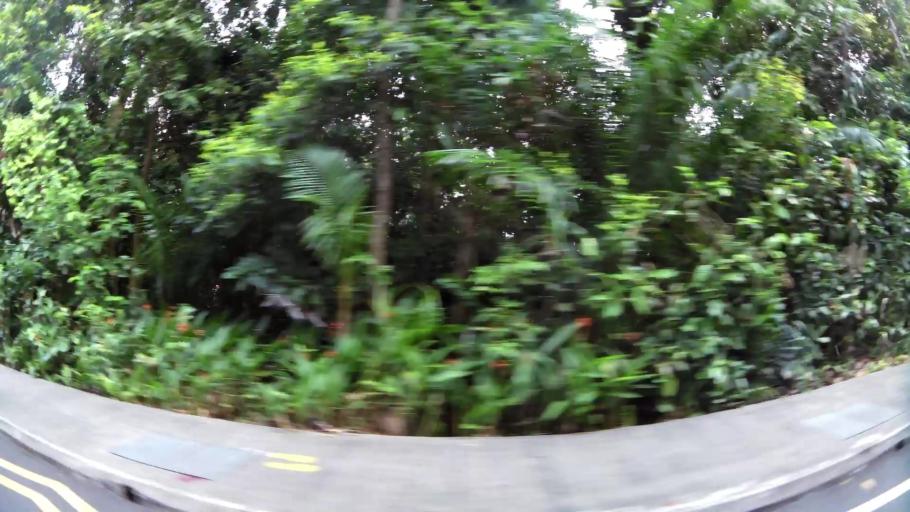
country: SG
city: Singapore
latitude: 1.2577
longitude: 103.8119
